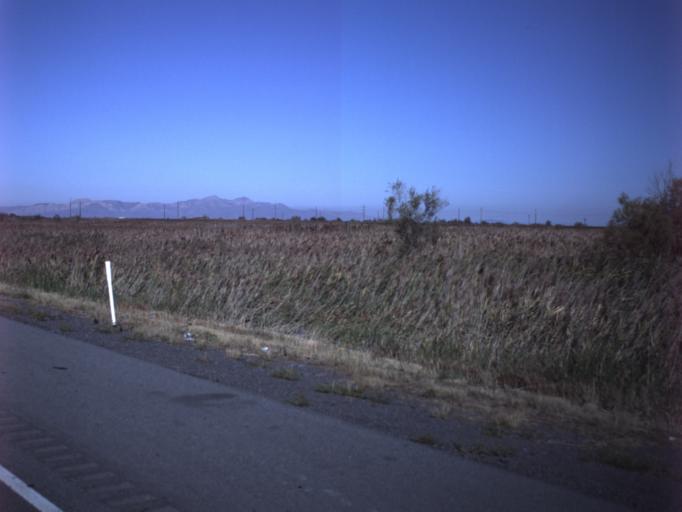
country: US
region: Utah
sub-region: Salt Lake County
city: Magna
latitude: 40.7279
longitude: -112.1796
